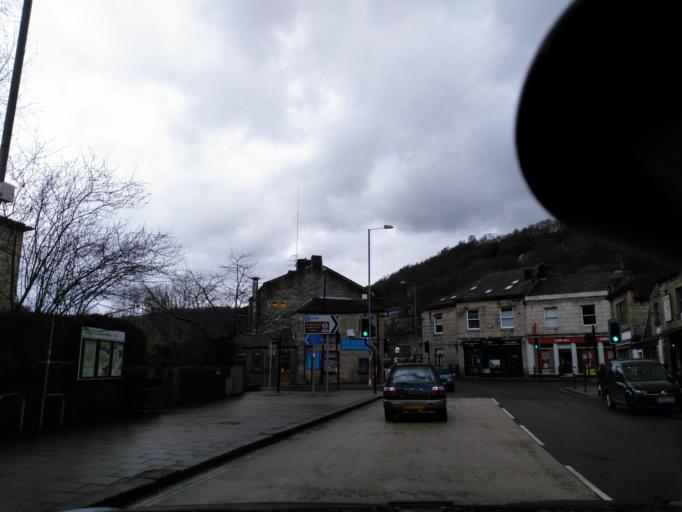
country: GB
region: England
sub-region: Calderdale
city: Hebden Bridge
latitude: 53.7410
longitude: -2.0133
